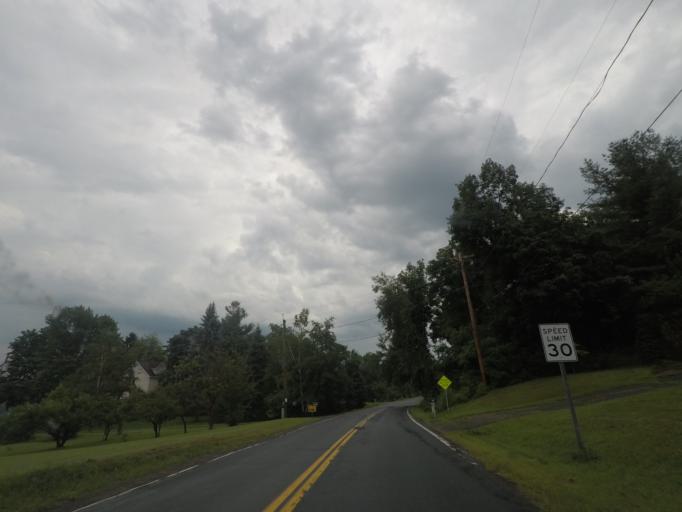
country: US
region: New York
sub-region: Rensselaer County
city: Poestenkill
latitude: 42.7558
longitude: -73.5906
